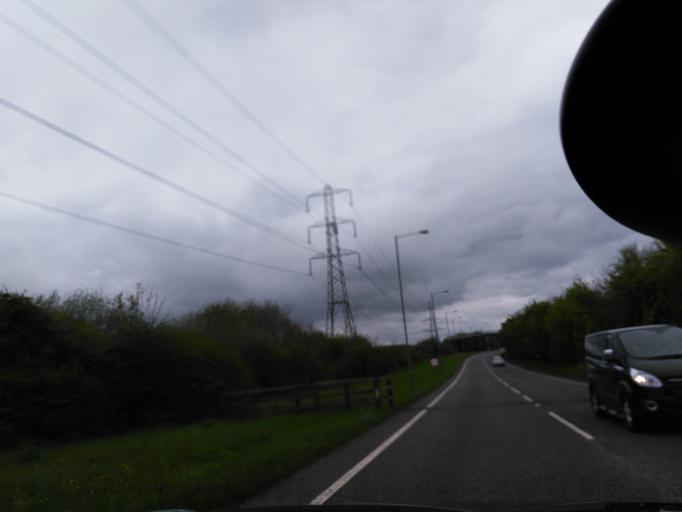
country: GB
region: England
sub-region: Wiltshire
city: Chippenham
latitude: 51.4601
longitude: -2.1507
